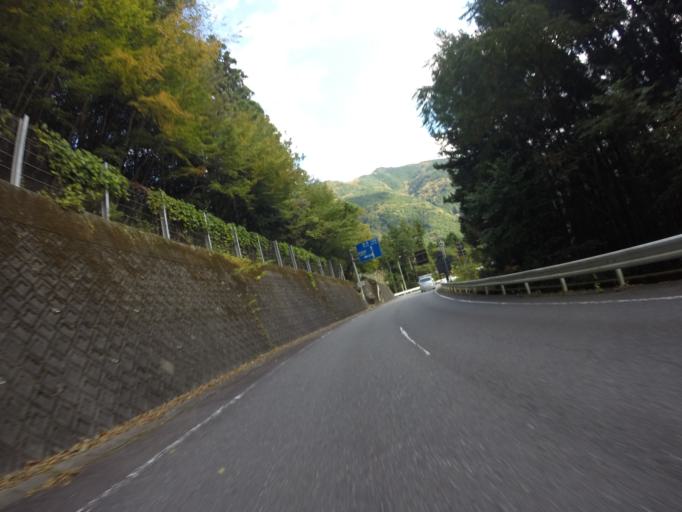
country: JP
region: Shizuoka
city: Shizuoka-shi
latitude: 35.1543
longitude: 138.1423
